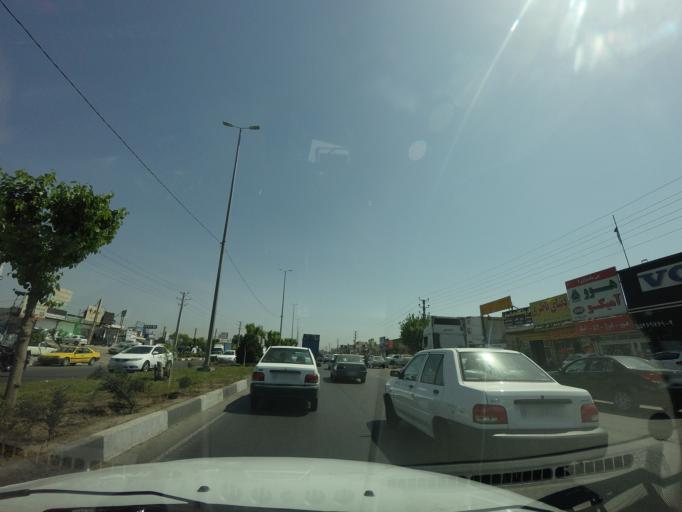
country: IR
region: Tehran
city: Eslamshahr
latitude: 35.5854
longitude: 51.2807
